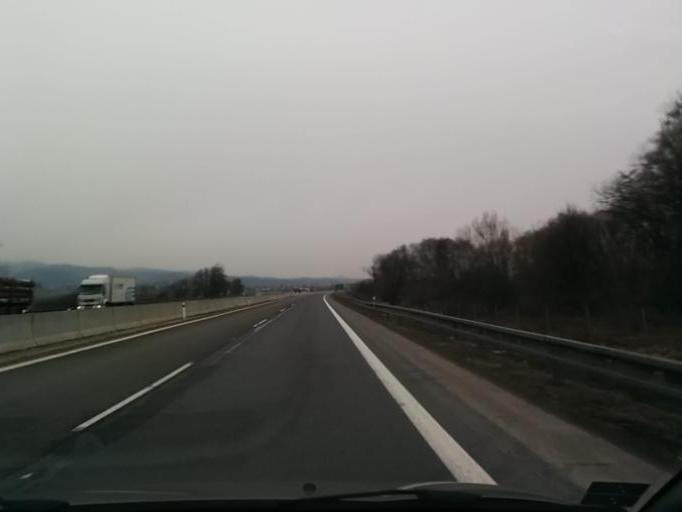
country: SK
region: Banskobystricky
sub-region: Okres Banska Bystrica
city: Zvolen
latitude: 48.6167
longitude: 19.1195
